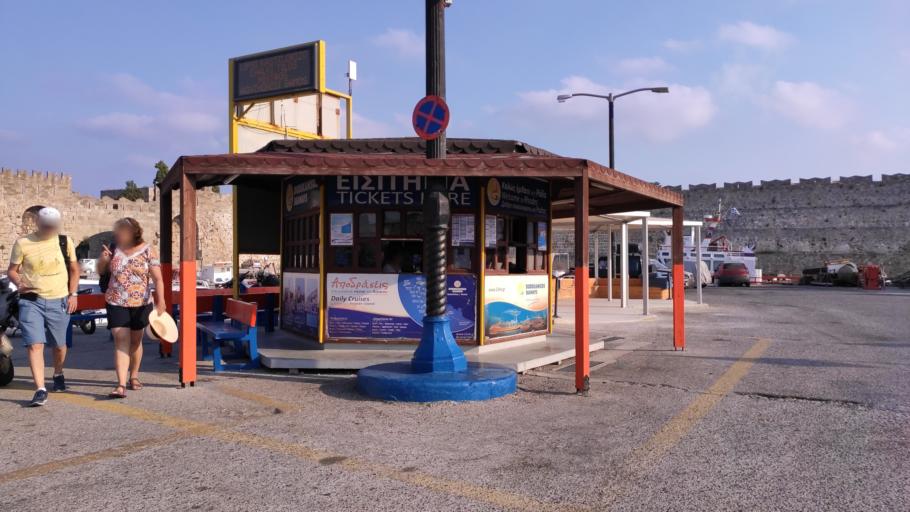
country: GR
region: South Aegean
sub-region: Nomos Dodekanisou
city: Rodos
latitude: 36.4454
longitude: 28.2288
